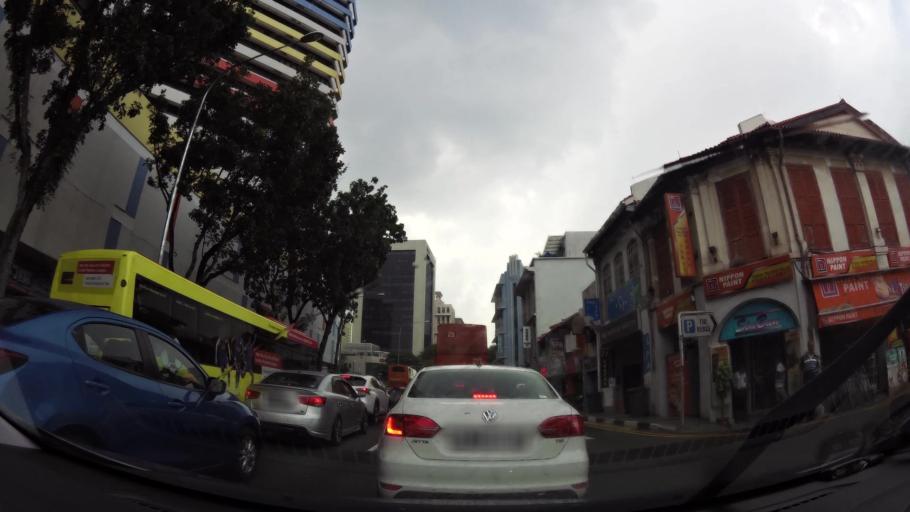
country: SG
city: Singapore
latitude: 1.3042
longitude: 103.8545
